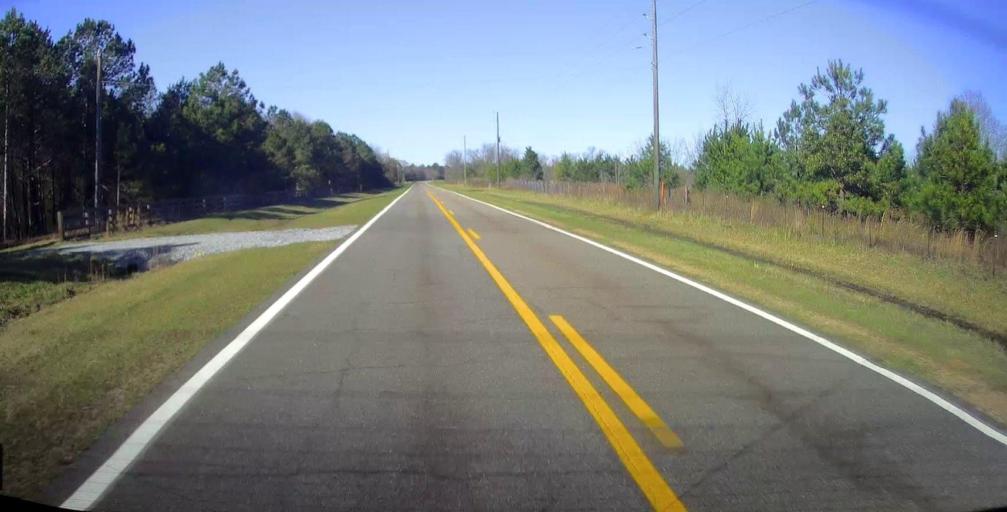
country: US
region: Georgia
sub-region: Peach County
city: Fort Valley
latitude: 32.5911
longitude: -83.9898
